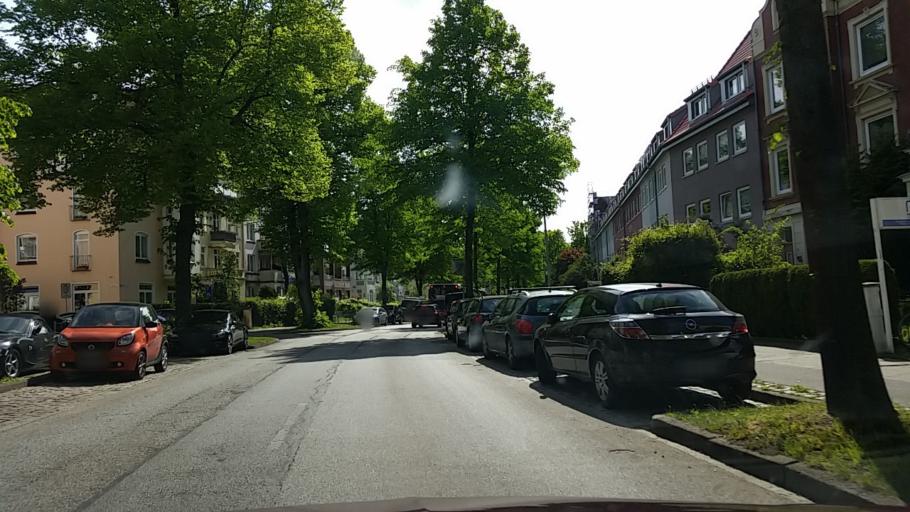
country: DE
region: Schleswig-Holstein
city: Luebeck
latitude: 53.8567
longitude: 10.6692
